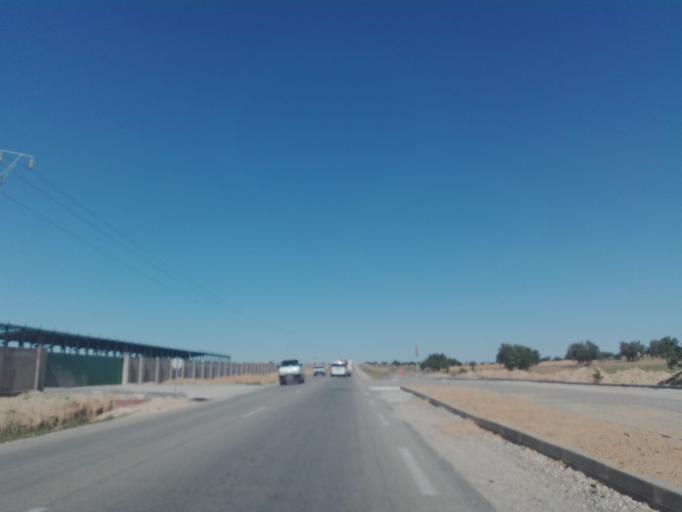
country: TN
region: Safaqis
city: Bi'r `Ali Bin Khalifah
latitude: 34.7348
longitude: 10.4155
